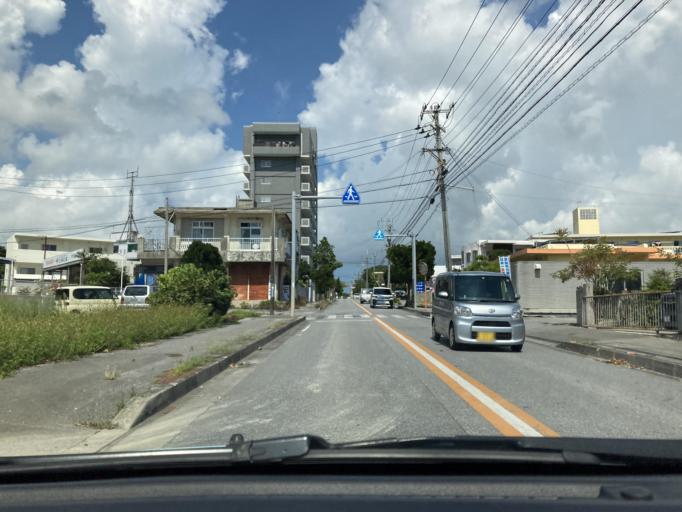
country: JP
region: Okinawa
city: Tomigusuku
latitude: 26.1587
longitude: 127.7471
